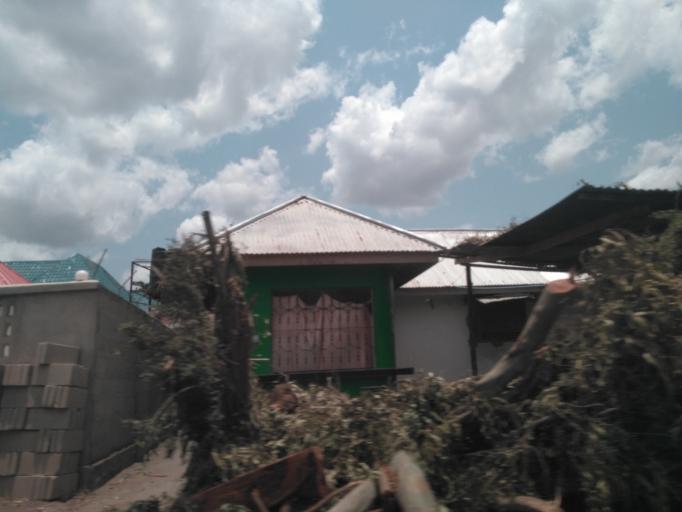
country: TZ
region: Dar es Salaam
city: Dar es Salaam
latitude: -6.8371
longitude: 39.3247
